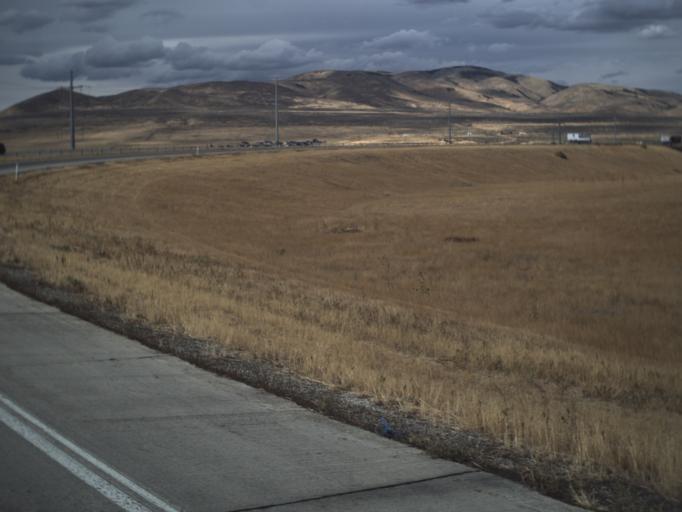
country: US
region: Utah
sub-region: Box Elder County
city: Tremonton
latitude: 41.7000
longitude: -112.1910
